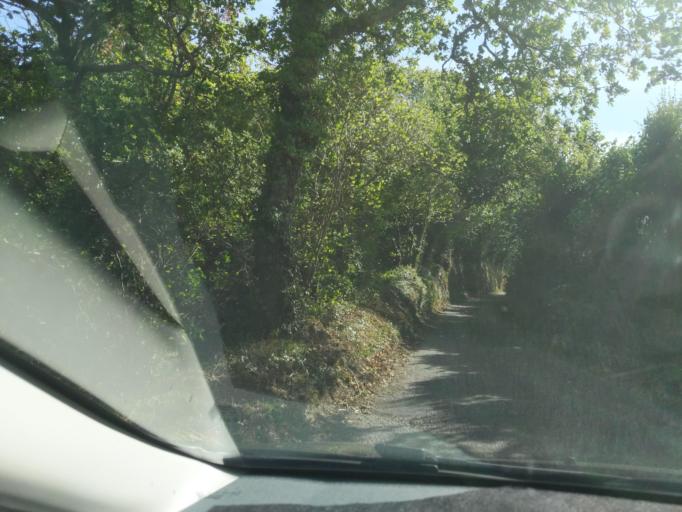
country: GB
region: England
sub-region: Cornwall
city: Torpoint
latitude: 50.3653
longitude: -4.2372
